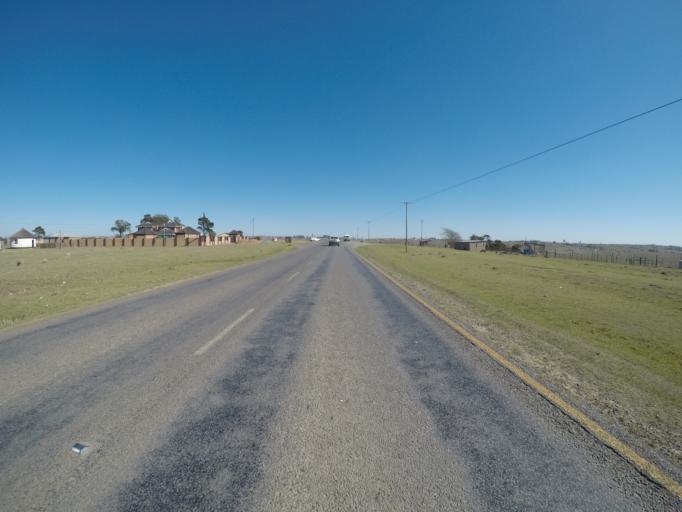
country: ZA
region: Eastern Cape
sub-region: OR Tambo District Municipality
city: Mthatha
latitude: -31.7845
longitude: 28.7410
